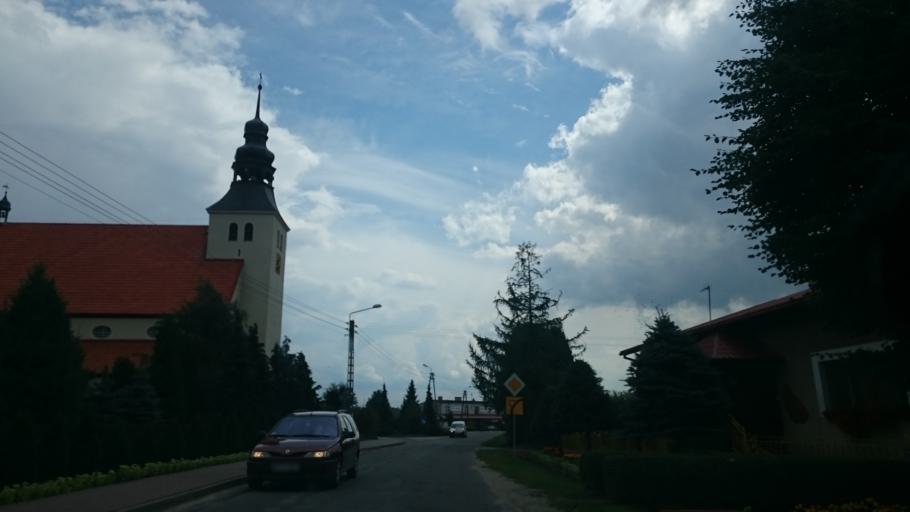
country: PL
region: Pomeranian Voivodeship
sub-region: Powiat chojnicki
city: Chojnice
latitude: 53.7004
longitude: 17.6846
